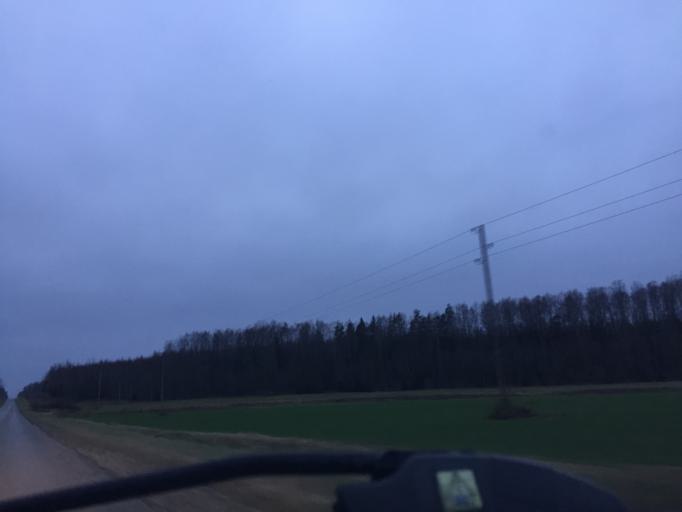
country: LV
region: Limbazu Rajons
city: Limbazi
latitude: 57.6079
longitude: 24.8147
